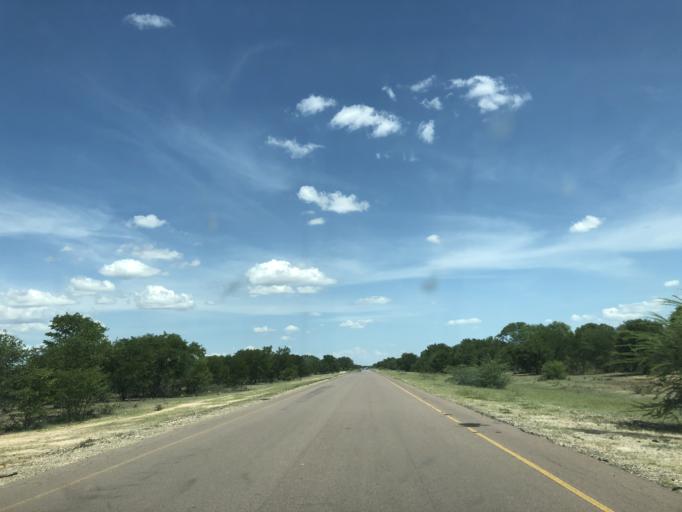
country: AO
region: Cunene
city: Ondjiva
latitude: -16.8162
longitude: 15.4389
